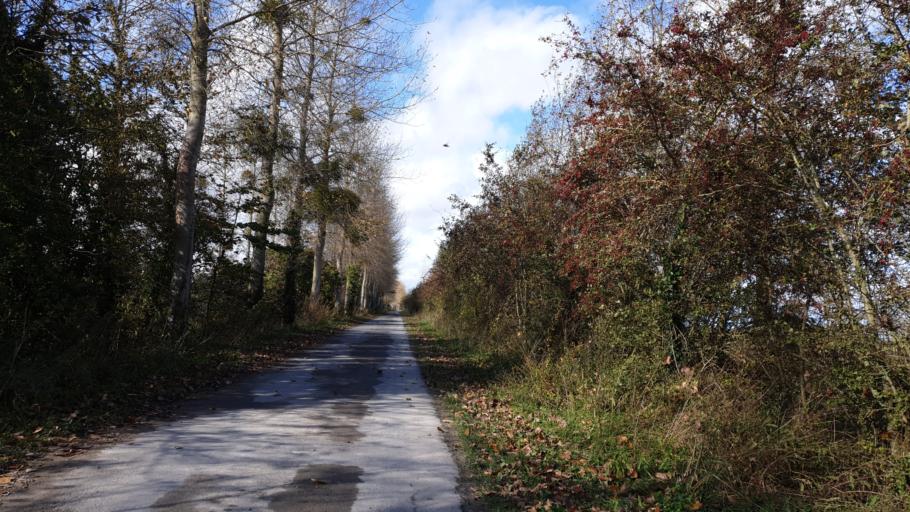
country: FR
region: Brittany
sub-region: Departement d'Ille-et-Vilaine
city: Saint-Broladre
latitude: 48.6072
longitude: -1.6423
